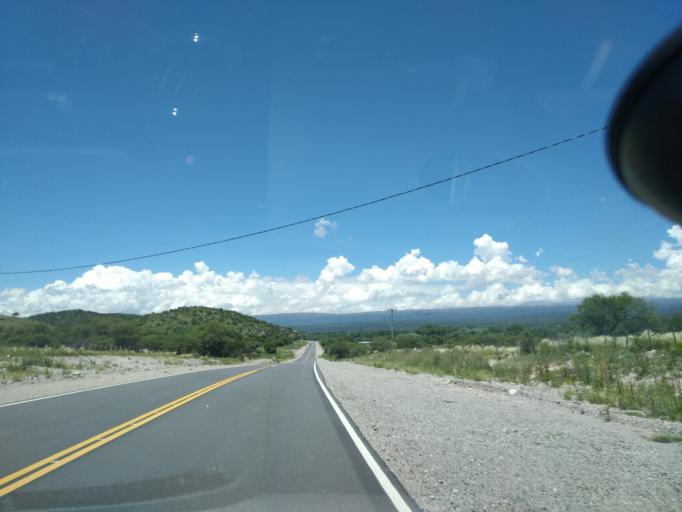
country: AR
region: Cordoba
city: Salsacate
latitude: -31.3485
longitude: -65.1134
